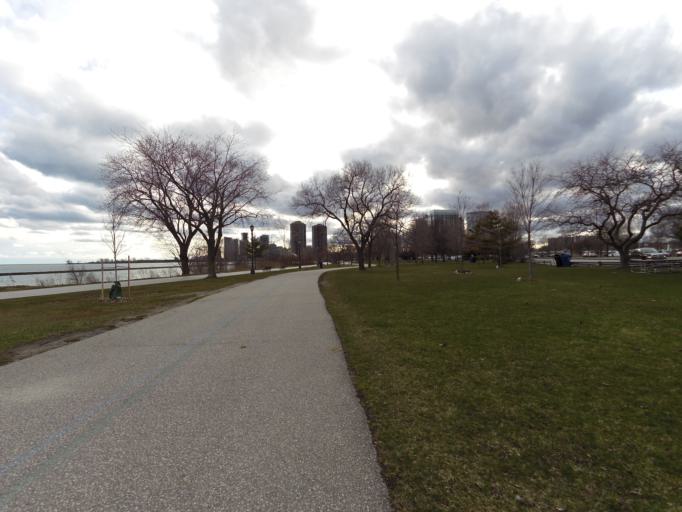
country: CA
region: Ontario
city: Toronto
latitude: 43.6371
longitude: -79.4602
